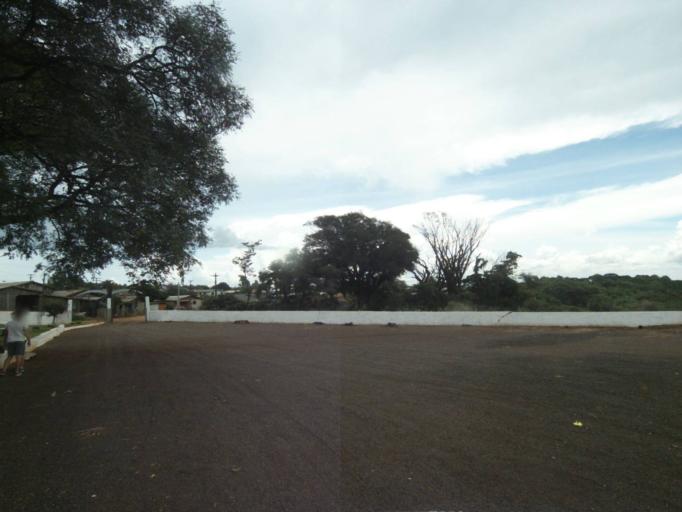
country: BR
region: Parana
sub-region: Guaraniacu
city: Guaraniacu
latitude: -25.1051
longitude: -52.8501
